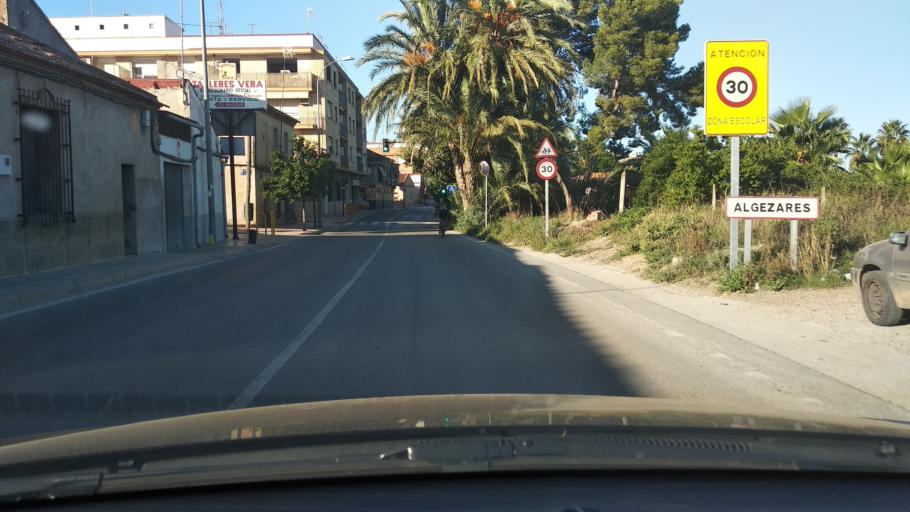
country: ES
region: Murcia
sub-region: Murcia
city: Murcia
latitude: 37.9462
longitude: -1.1079
